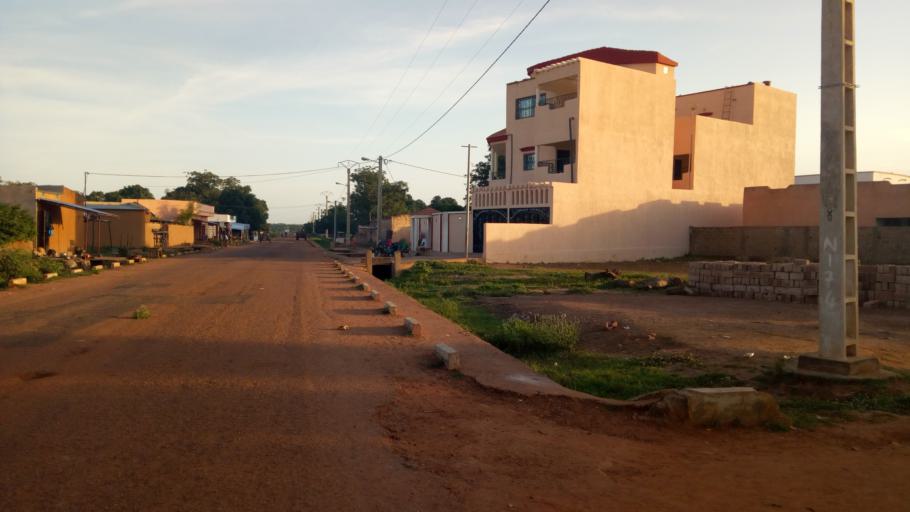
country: ML
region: Sikasso
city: Koutiala
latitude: 12.4075
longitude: -5.4450
